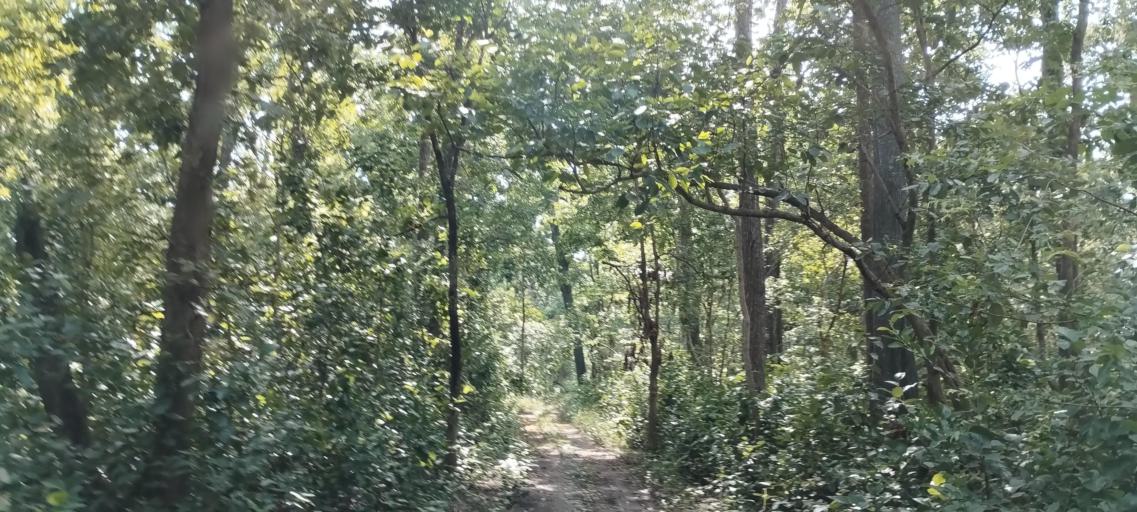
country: NP
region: Far Western
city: Tikapur
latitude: 28.5666
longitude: 81.2859
